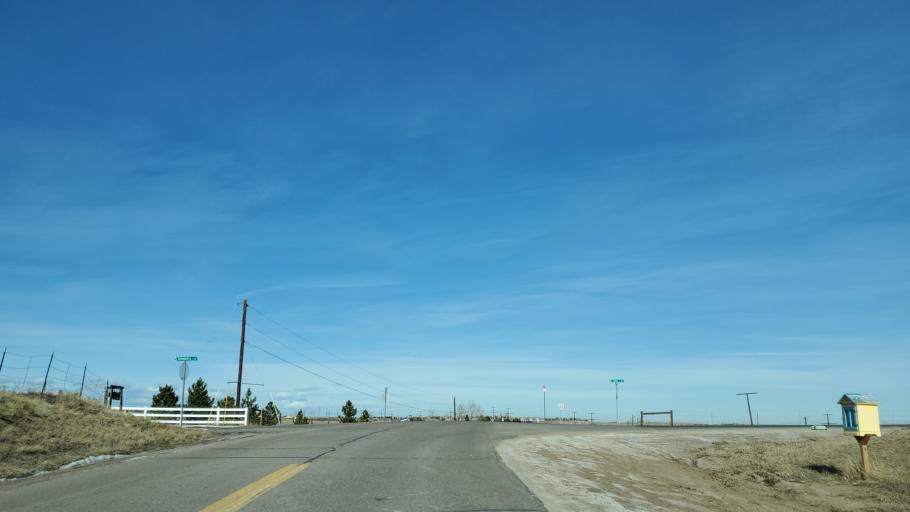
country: US
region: Colorado
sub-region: Douglas County
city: Castle Pines
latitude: 39.4474
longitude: -104.8724
